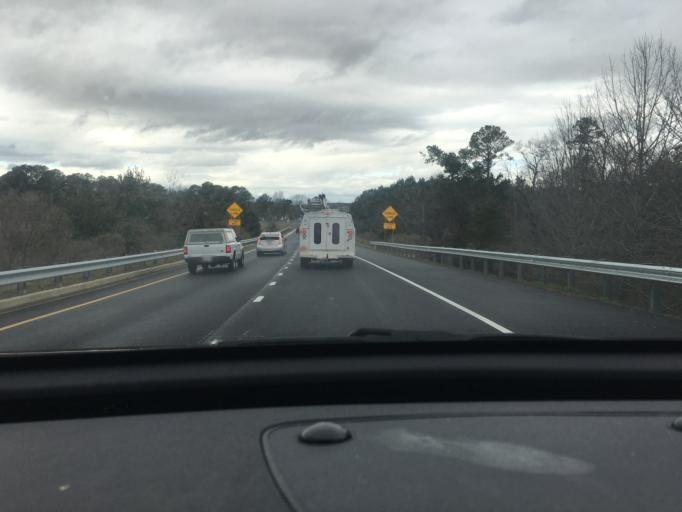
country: US
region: Maryland
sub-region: Wicomico County
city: Salisbury
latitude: 38.4024
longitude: -75.6307
